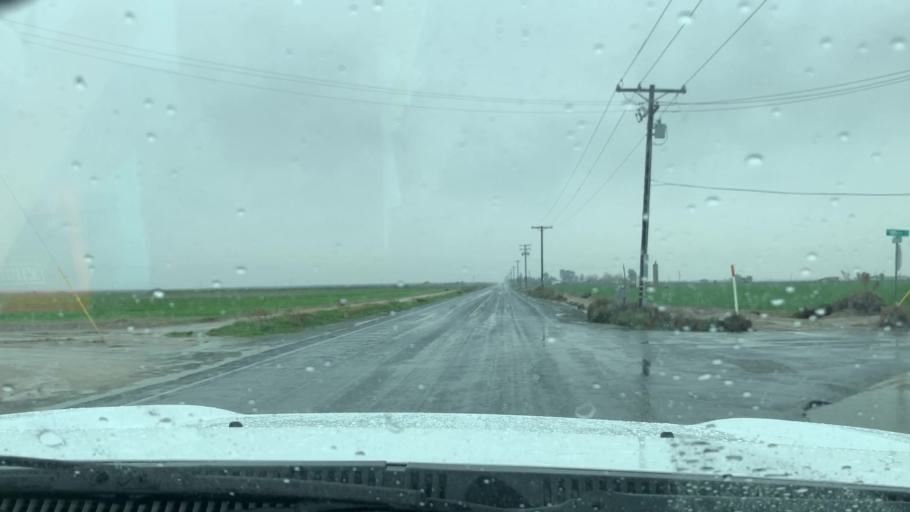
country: US
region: California
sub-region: Tulare County
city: Earlimart
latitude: 35.8919
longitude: -119.3037
